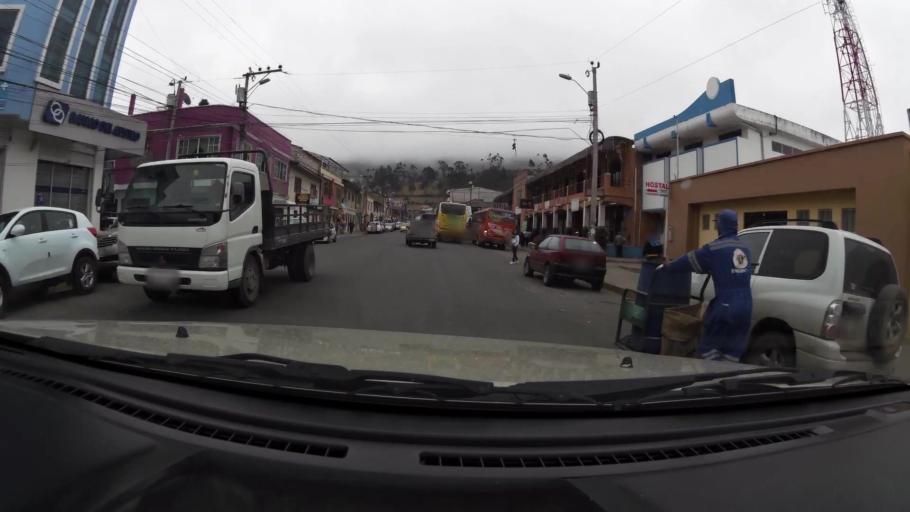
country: EC
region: Canar
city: Canar
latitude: -2.5100
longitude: -78.9276
